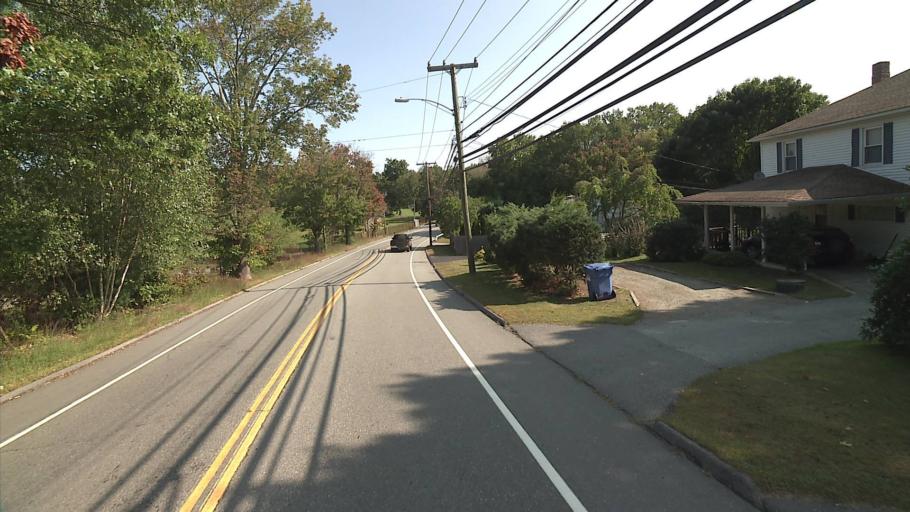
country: US
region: Connecticut
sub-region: New London County
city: Norwich
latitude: 41.5629
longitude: -72.0665
